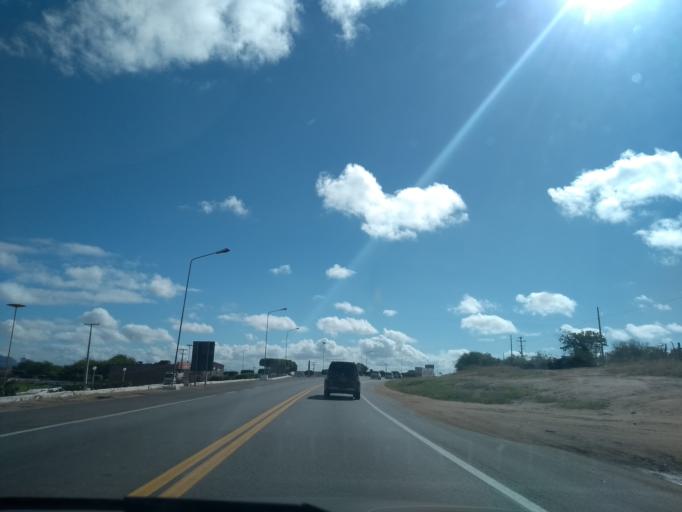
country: BR
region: Bahia
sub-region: Amargosa
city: Amargosa
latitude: -12.8677
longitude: -39.8556
